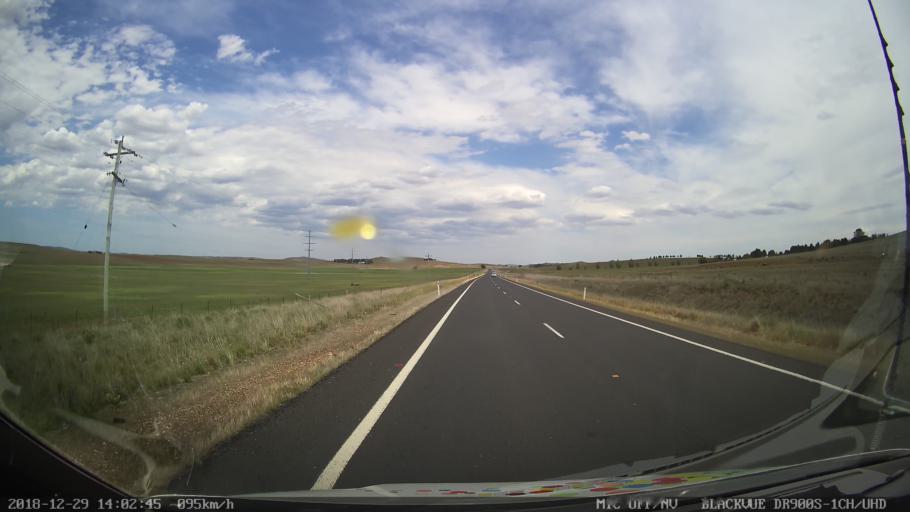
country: AU
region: New South Wales
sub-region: Cooma-Monaro
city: Cooma
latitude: -36.2920
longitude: 149.1796
